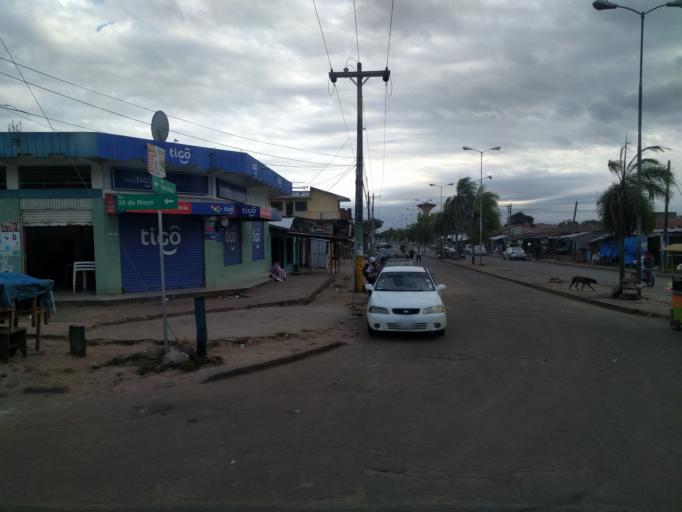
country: BO
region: Santa Cruz
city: Warnes
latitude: -17.5150
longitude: -63.1657
